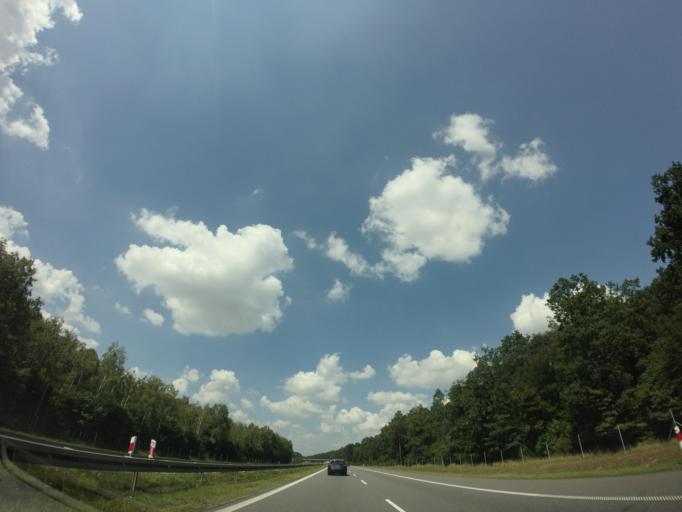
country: PL
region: Opole Voivodeship
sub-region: Powiat opolski
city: Proszkow
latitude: 50.5461
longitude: 17.8953
